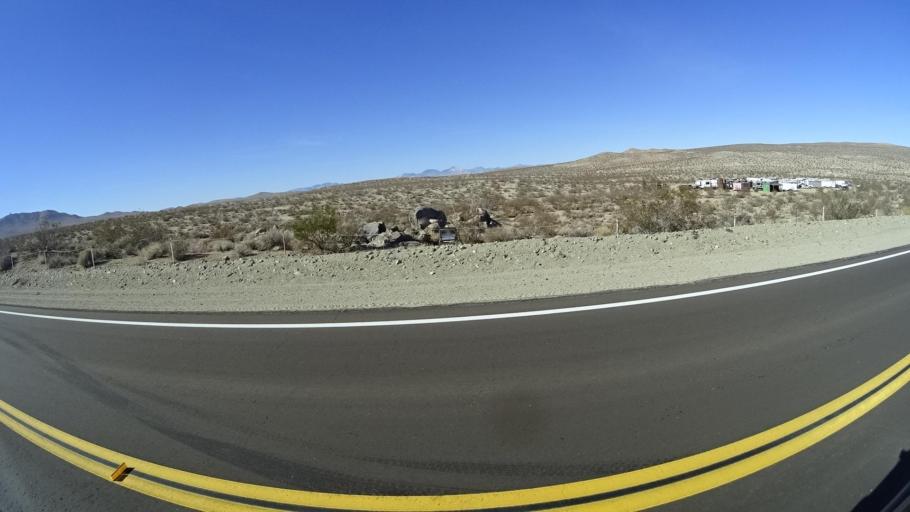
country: US
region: California
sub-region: Kern County
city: Ridgecrest
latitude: 35.5006
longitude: -117.6224
